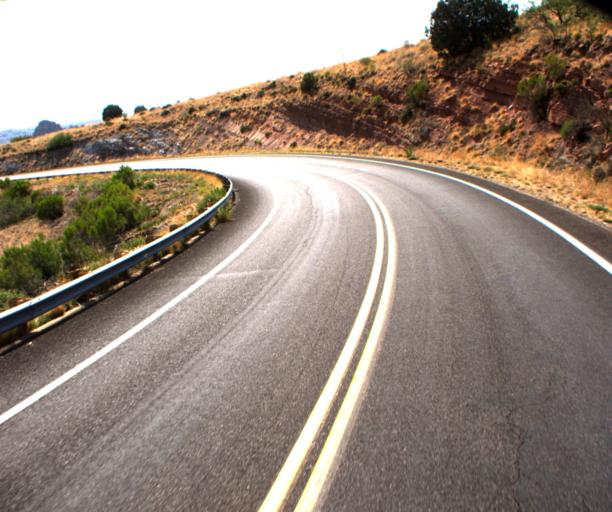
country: US
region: Arizona
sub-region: Greenlee County
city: Clifton
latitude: 33.0482
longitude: -109.1071
